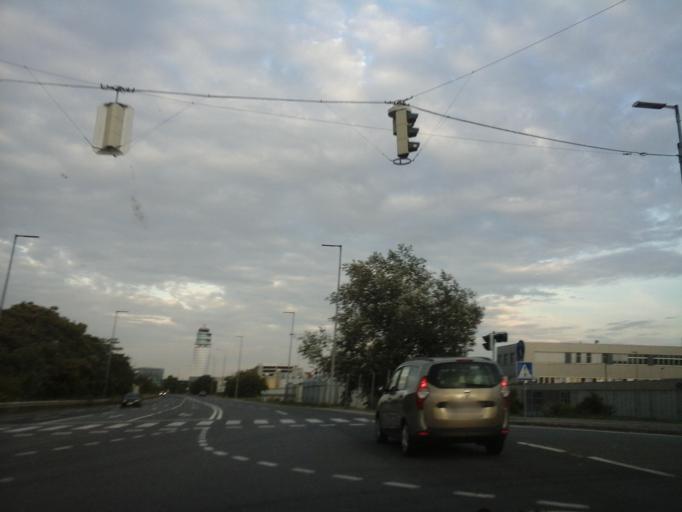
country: AT
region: Lower Austria
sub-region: Politischer Bezirk Wien-Umgebung
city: Rauchenwarth
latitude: 48.1269
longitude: 16.5490
